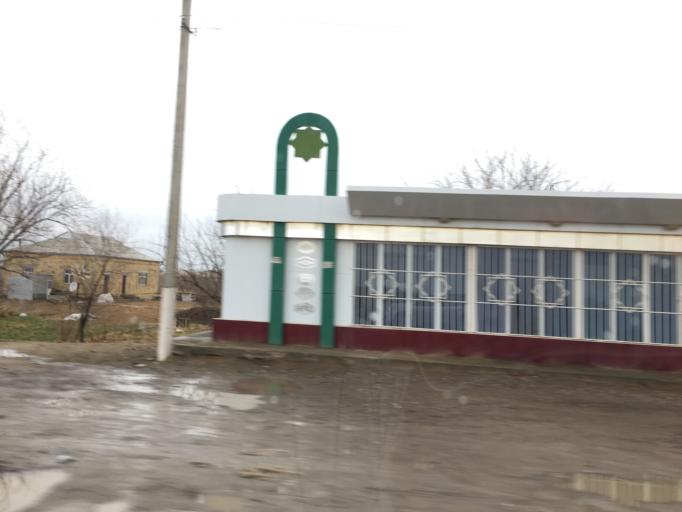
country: TM
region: Mary
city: Yoloeten
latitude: 37.2881
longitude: 62.3495
